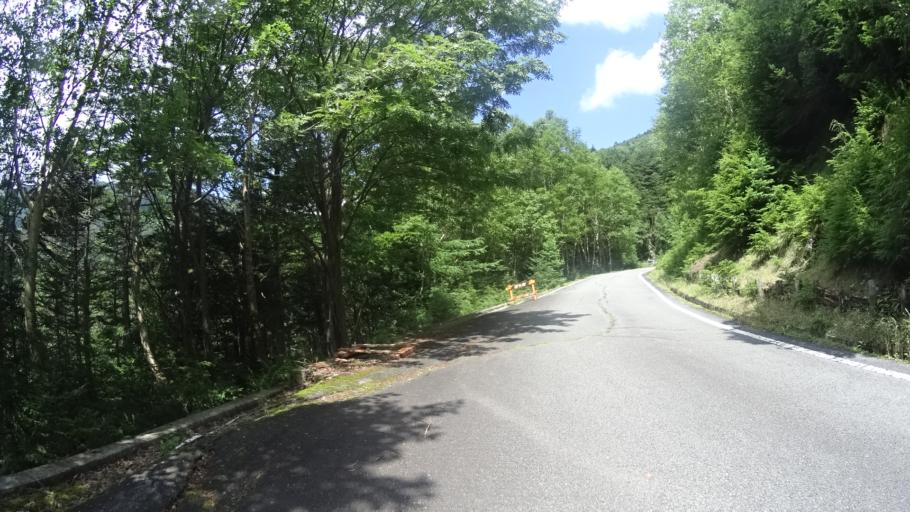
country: JP
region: Yamanashi
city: Enzan
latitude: 35.8621
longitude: 138.6570
